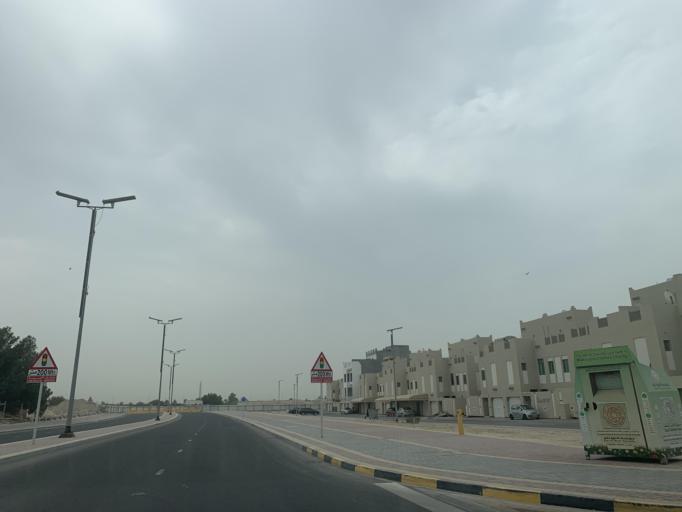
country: BH
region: Northern
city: Madinat `Isa
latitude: 26.1684
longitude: 50.5117
